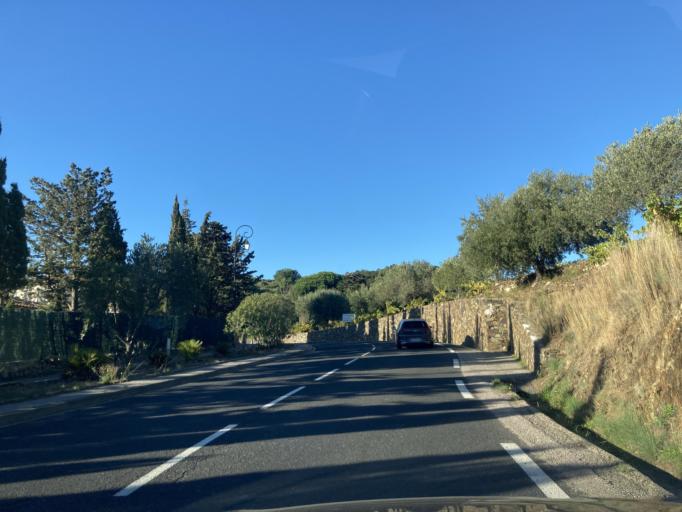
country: FR
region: Languedoc-Roussillon
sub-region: Departement des Pyrenees-Orientales
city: Collioure
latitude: 42.5277
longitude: 3.0747
